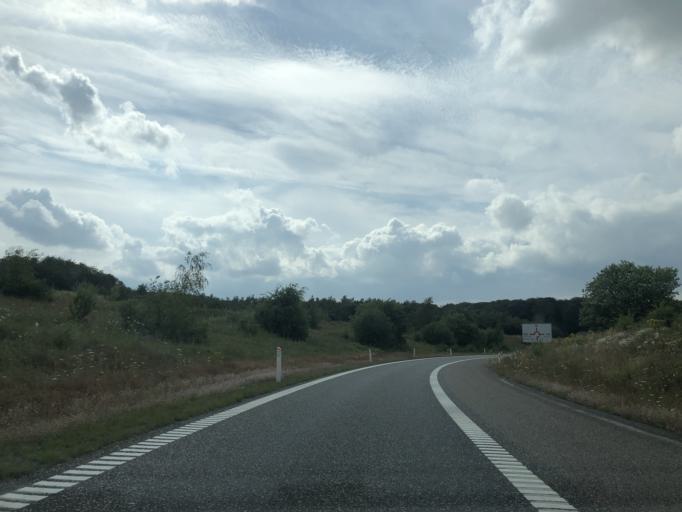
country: DK
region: Central Jutland
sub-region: Skanderborg Kommune
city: Skovby
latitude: 56.1490
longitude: 9.9699
